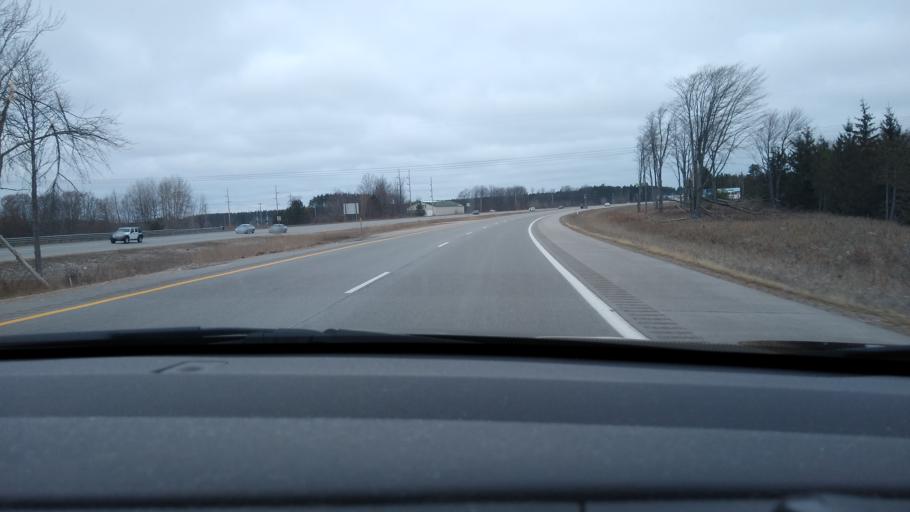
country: US
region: Michigan
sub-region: Otsego County
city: Gaylord
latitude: 44.9938
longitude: -84.6843
